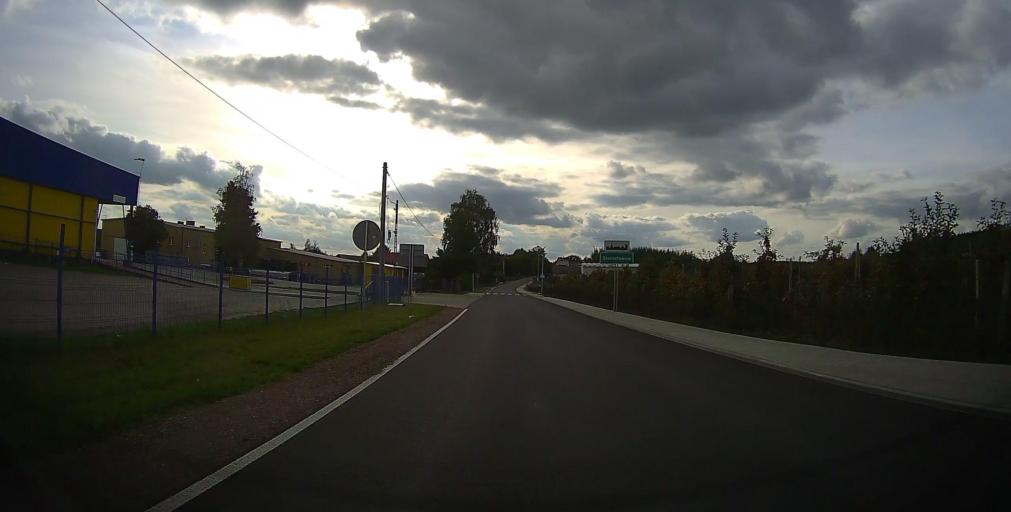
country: PL
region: Masovian Voivodeship
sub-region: Powiat bialobrzeski
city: Promna
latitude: 51.7082
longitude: 20.9533
